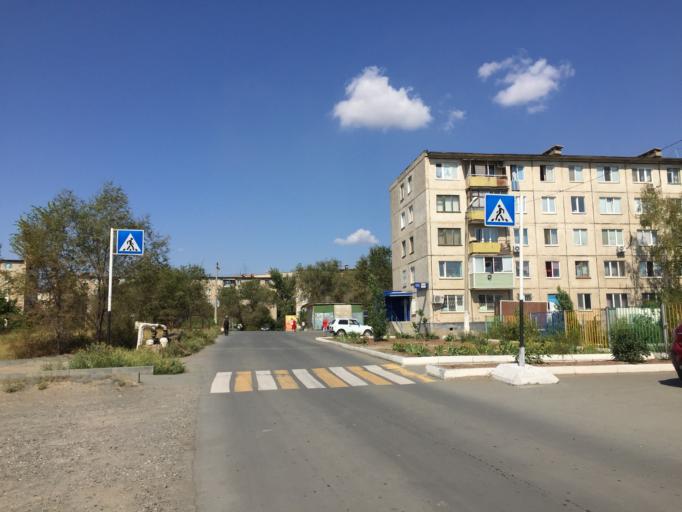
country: RU
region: Orenburg
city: Novotroitsk
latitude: 51.1956
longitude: 58.2860
